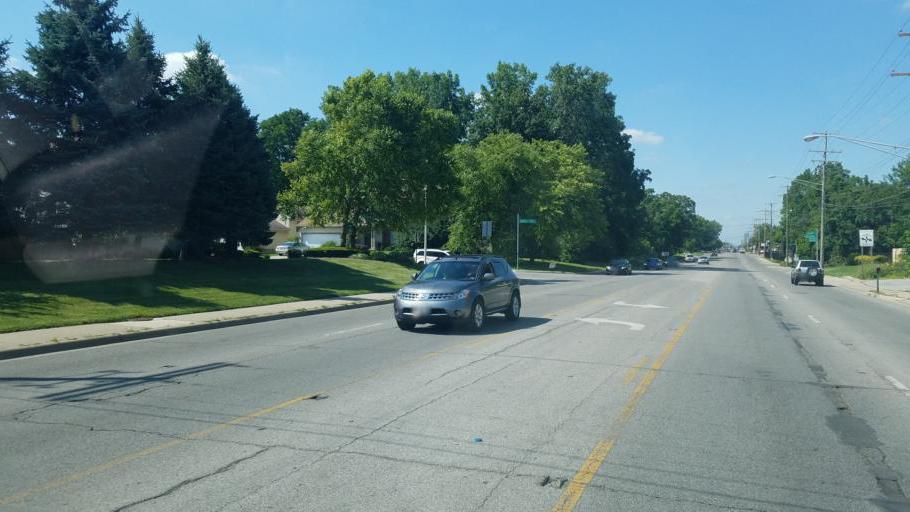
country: US
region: Ohio
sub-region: Franklin County
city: Minerva Park
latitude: 40.0733
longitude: -82.9519
